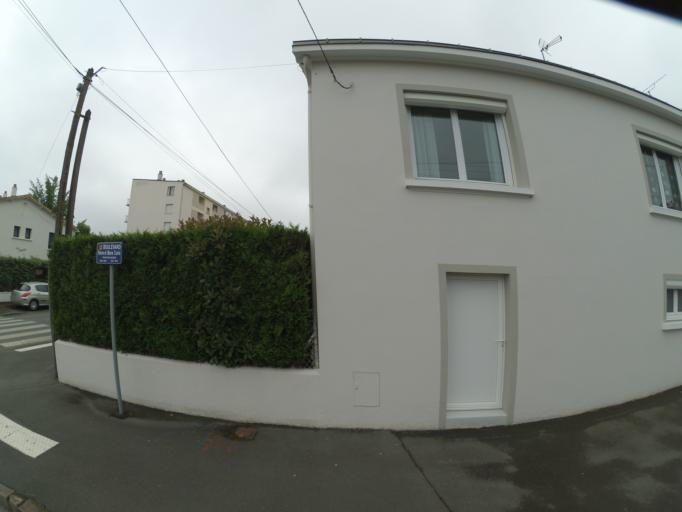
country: FR
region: Pays de la Loire
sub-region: Departement de la Vendee
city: La Roche-sur-Yon
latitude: 46.6651
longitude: -1.4328
